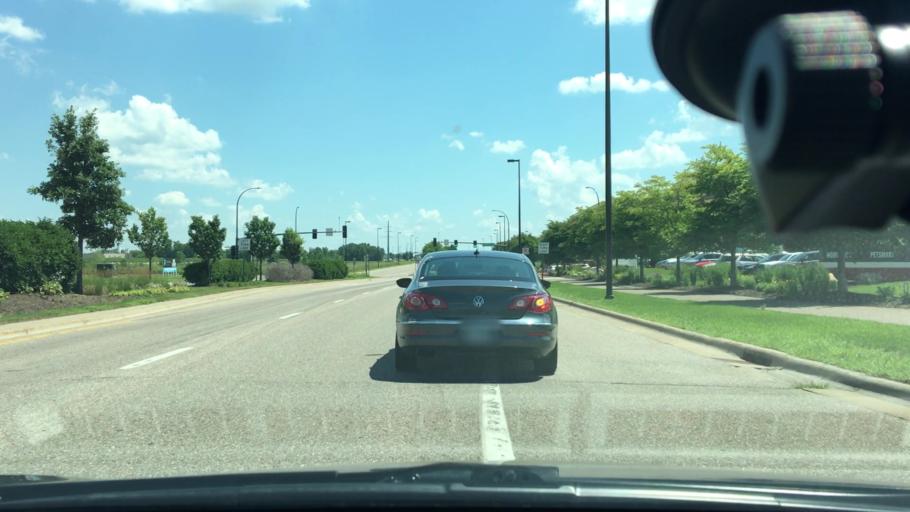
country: US
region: Minnesota
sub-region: Hennepin County
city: Maple Grove
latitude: 45.0946
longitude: -93.4288
